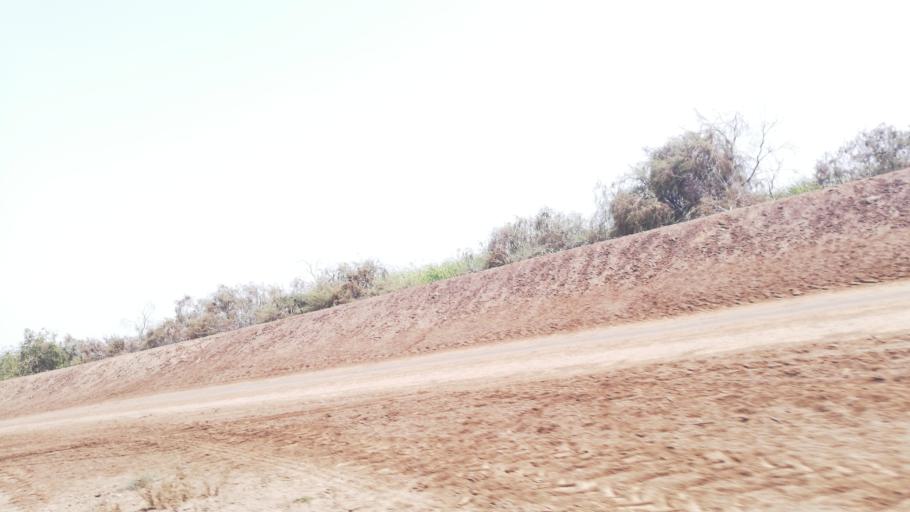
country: SN
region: Saint-Louis
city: Saint-Louis
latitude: 16.4032
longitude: -16.2931
